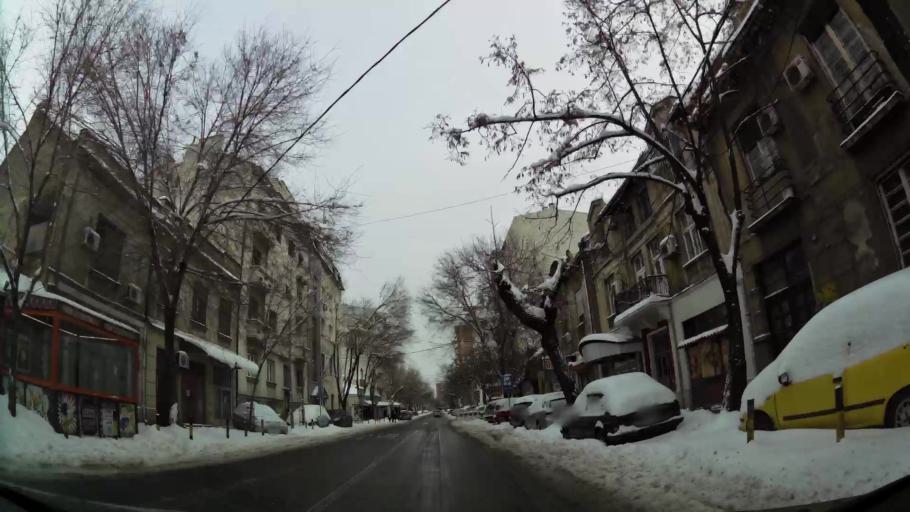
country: RS
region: Central Serbia
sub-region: Belgrade
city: Stari Grad
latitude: 44.8199
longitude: 20.4705
